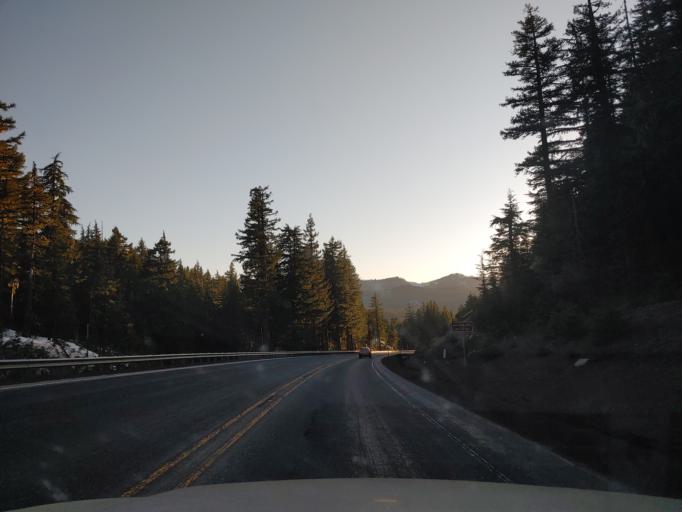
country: US
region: Oregon
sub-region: Lane County
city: Oakridge
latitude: 43.6123
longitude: -122.1066
